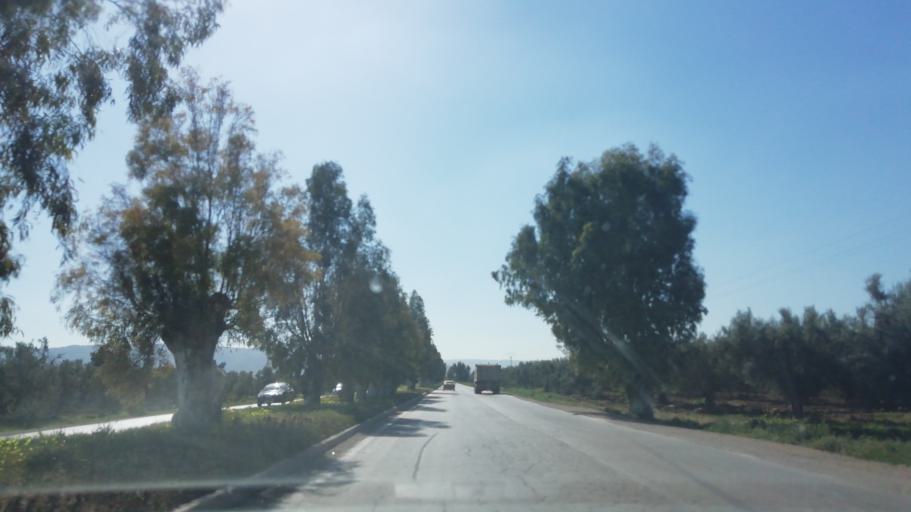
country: DZ
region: Mascara
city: Sig
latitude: 35.5585
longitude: -0.2073
